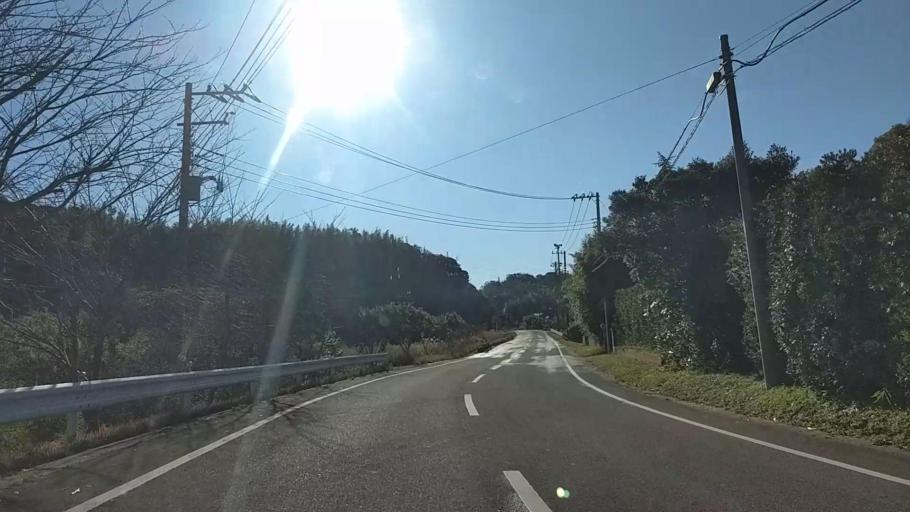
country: JP
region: Chiba
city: Futtsu
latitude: 35.2409
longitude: 139.8747
